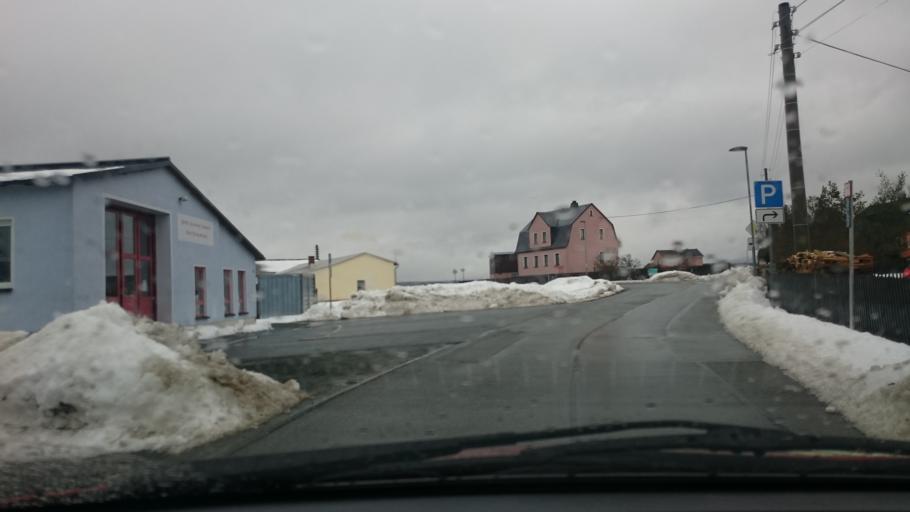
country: DE
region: Saxony
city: Markneukirchen
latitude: 50.2725
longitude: 12.3289
